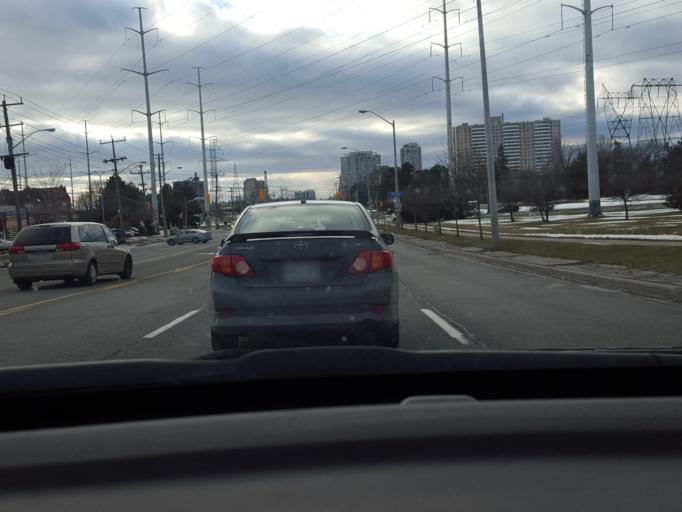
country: CA
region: Ontario
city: Scarborough
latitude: 43.7540
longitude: -79.2536
